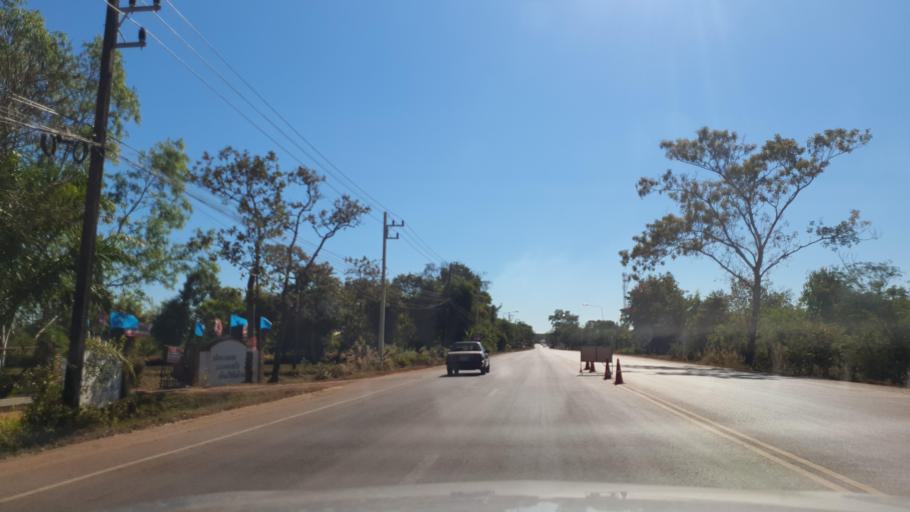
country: TH
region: Nakhon Phanom
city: Si Songkhram
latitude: 17.7648
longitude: 104.2795
